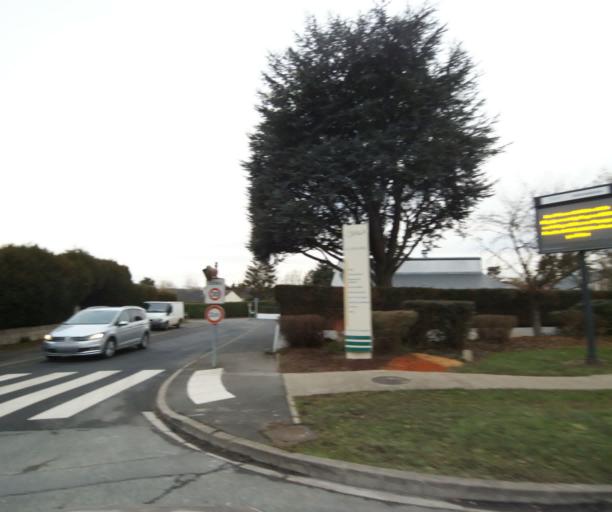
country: FR
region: Ile-de-France
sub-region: Departement de Seine-et-Marne
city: Othis
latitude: 49.0715
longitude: 2.6770
